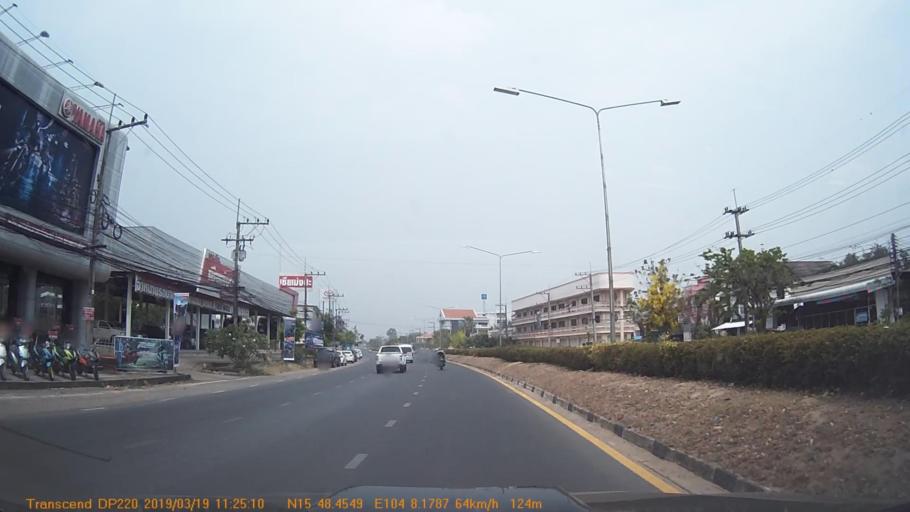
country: TH
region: Yasothon
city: Yasothon
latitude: 15.8077
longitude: 104.1362
